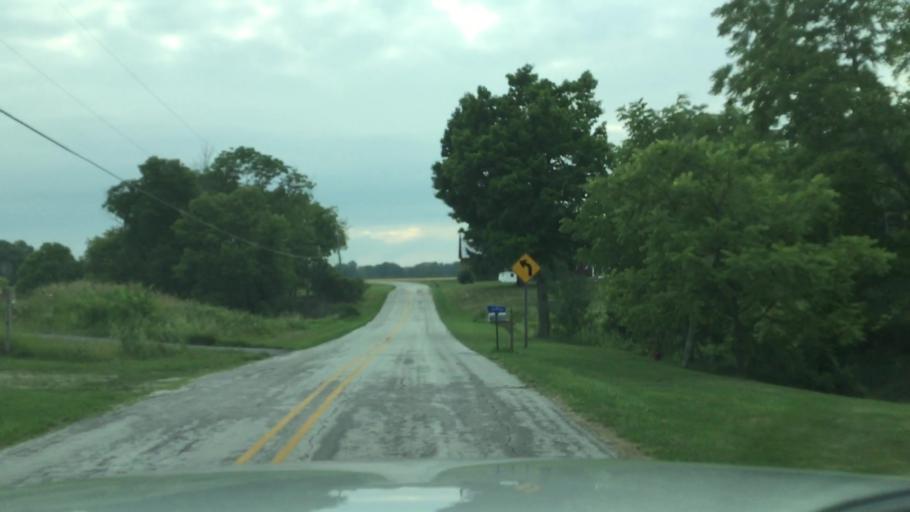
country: US
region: Michigan
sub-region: Saginaw County
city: Frankenmuth
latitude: 43.3334
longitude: -83.7834
